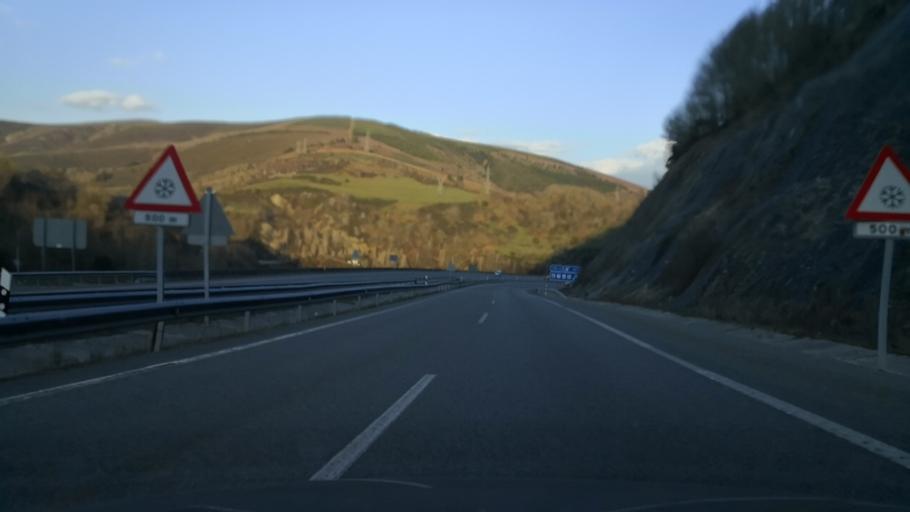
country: ES
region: Castille and Leon
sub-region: Provincia de Leon
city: Vega de Valcarce
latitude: 42.6643
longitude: -6.9357
